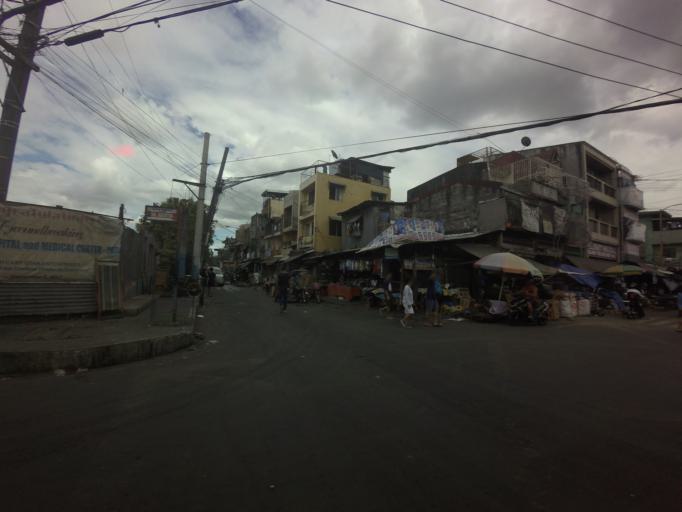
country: PH
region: Calabarzon
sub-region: Province of Rizal
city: Pateros
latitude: 14.5591
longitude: 121.0853
